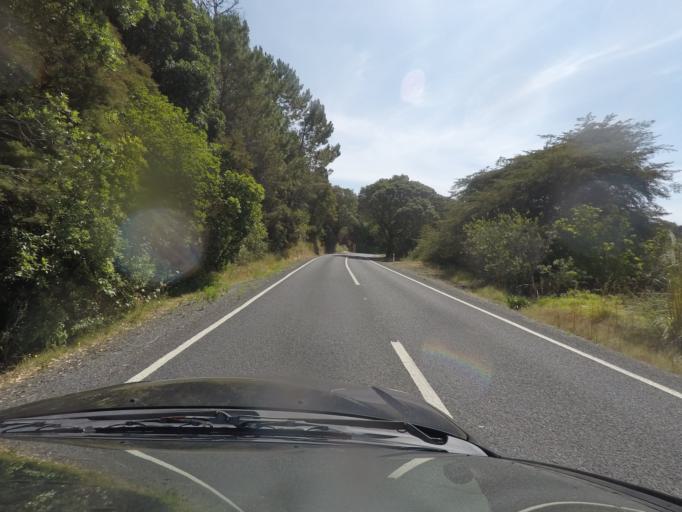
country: NZ
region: Auckland
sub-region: Auckland
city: Warkworth
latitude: -36.3059
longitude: 174.7829
